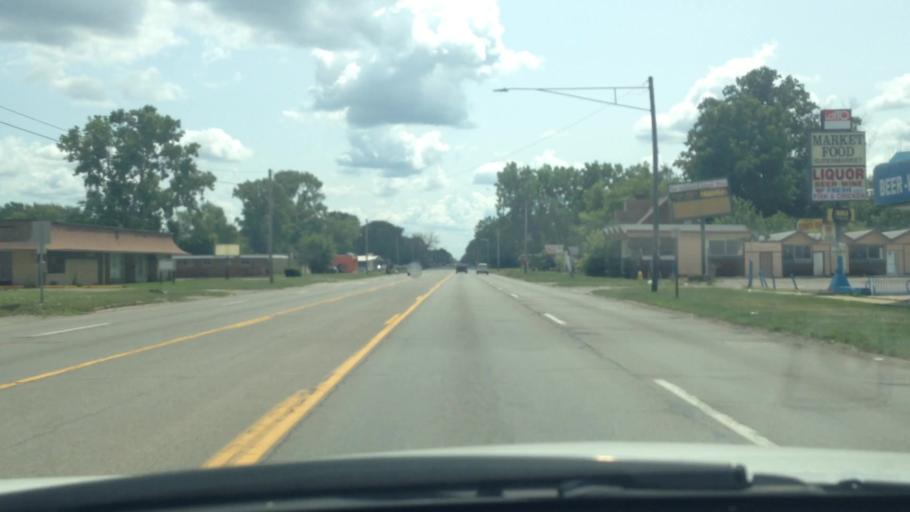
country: US
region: Michigan
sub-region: Wayne County
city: Inkster
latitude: 42.2822
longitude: -83.3096
